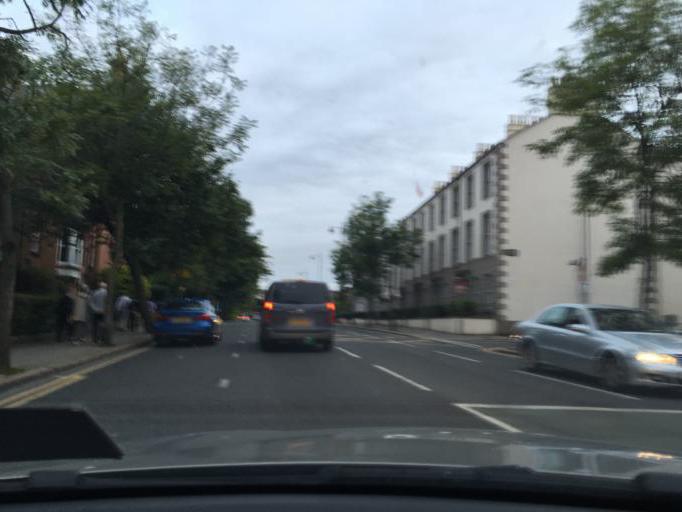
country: GB
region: Northern Ireland
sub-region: City of Belfast
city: Belfast
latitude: 54.5860
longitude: -5.9360
